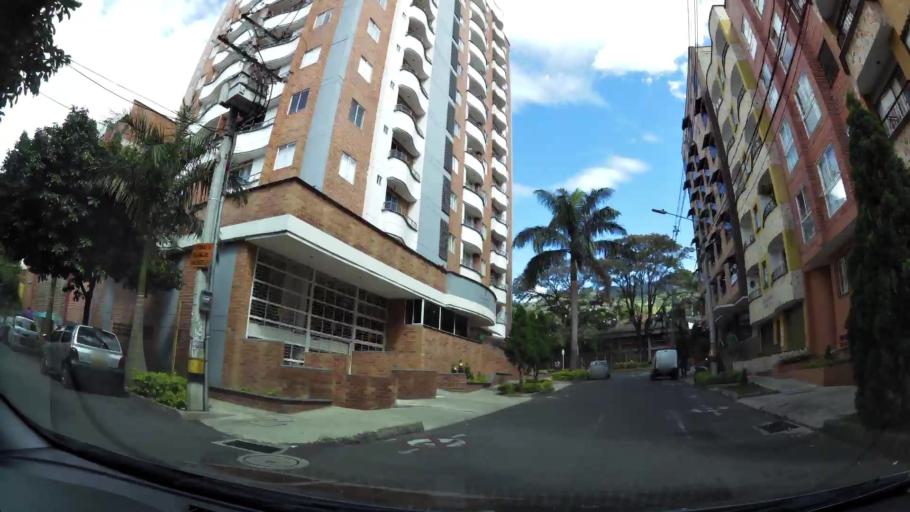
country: CO
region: Antioquia
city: Sabaneta
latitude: 6.1538
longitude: -75.6108
